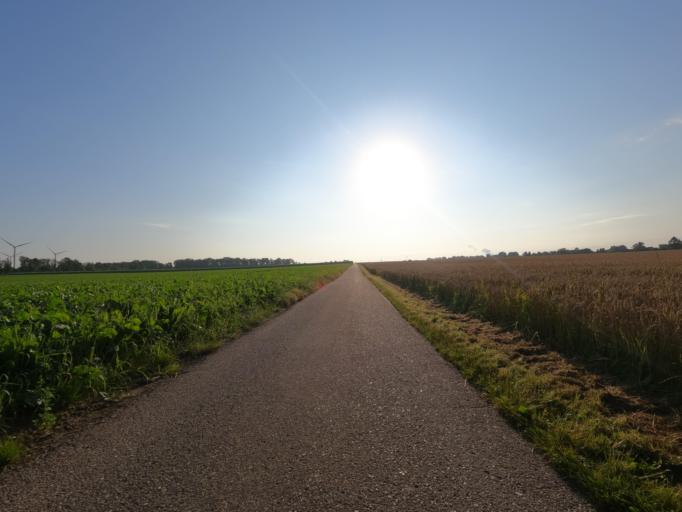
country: DE
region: North Rhine-Westphalia
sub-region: Regierungsbezirk Koln
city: Titz
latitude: 51.0108
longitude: 6.4160
